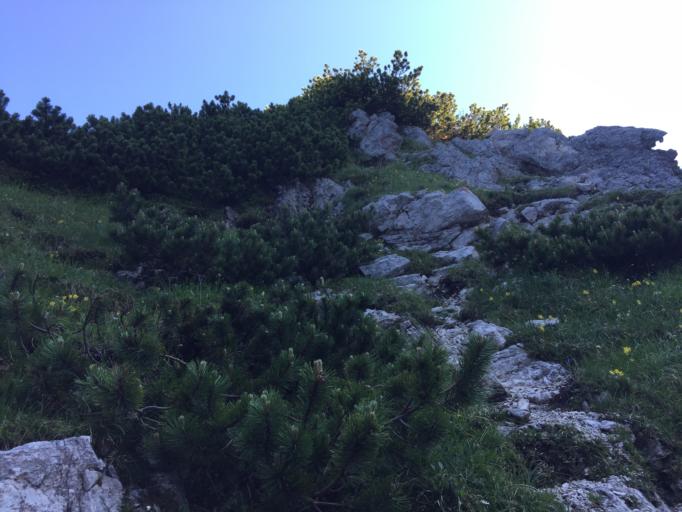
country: IT
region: Friuli Venezia Giulia
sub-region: Provincia di Udine
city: Pontebba
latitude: 46.4724
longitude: 13.2444
